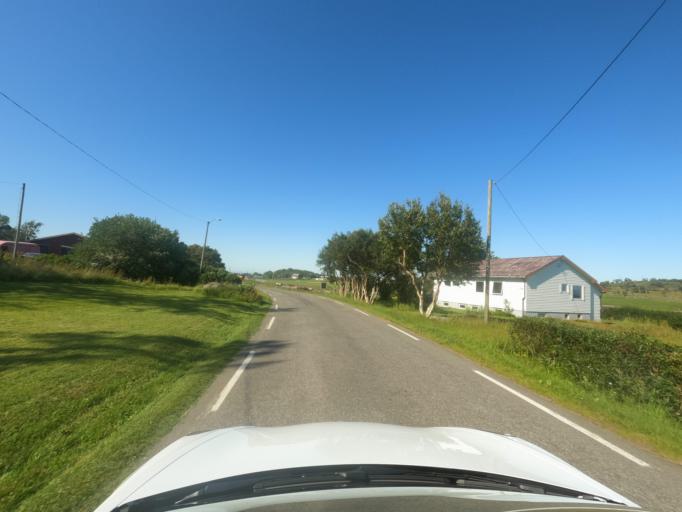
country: NO
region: Nordland
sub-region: Hadsel
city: Melbu
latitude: 68.4344
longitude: 14.7486
